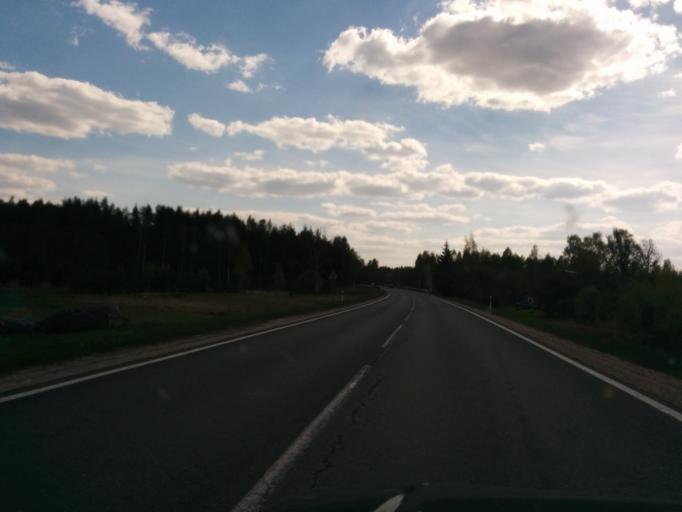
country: LV
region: Pargaujas
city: Stalbe
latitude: 57.3322
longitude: 24.9242
